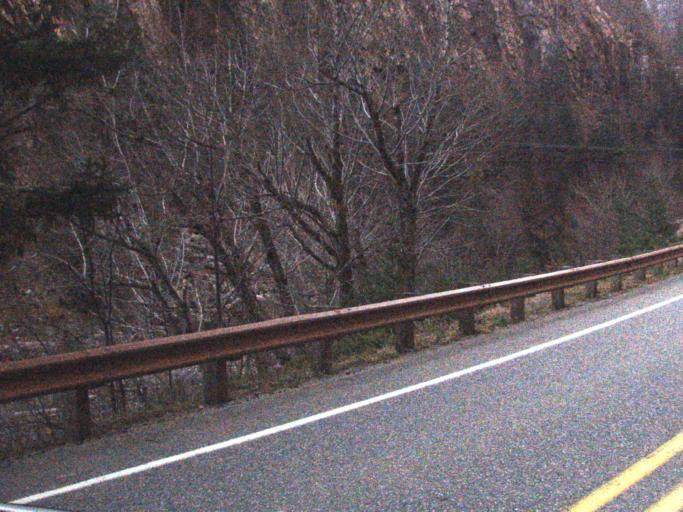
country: US
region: Washington
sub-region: Snohomish County
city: Darrington
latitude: 48.6875
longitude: -121.2373
